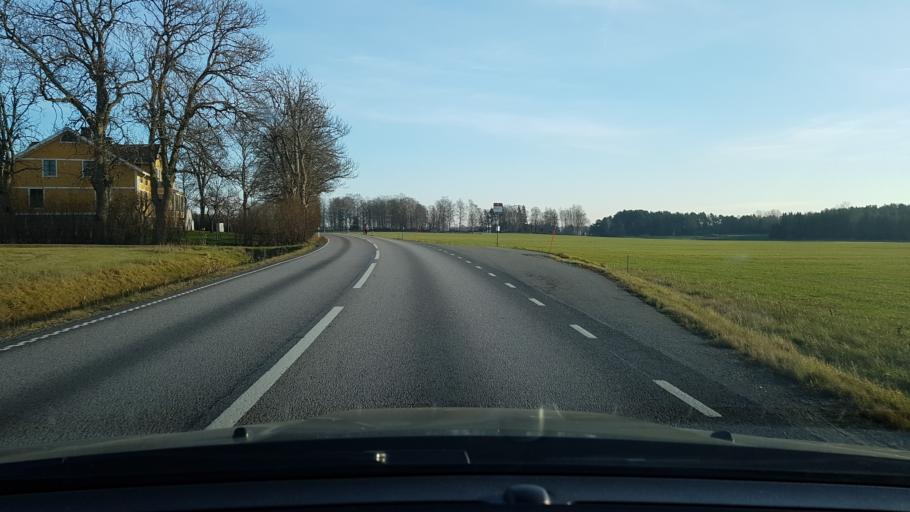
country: SE
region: Stockholm
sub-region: Norrtalje Kommun
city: Nykvarn
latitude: 59.7426
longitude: 18.1323
